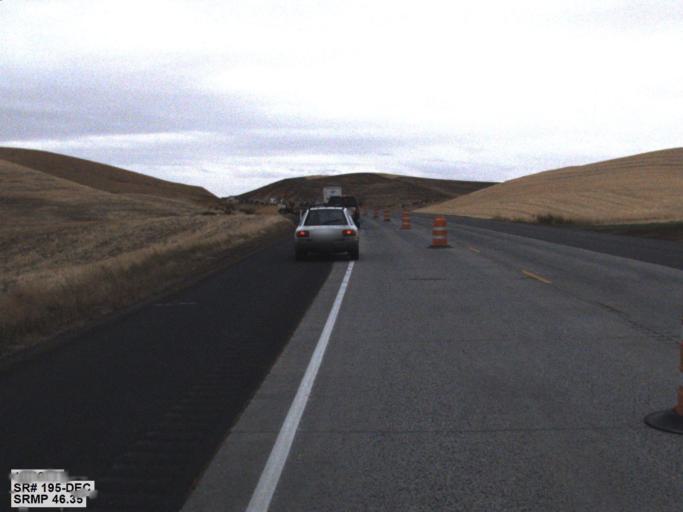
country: US
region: Washington
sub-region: Whitman County
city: Colfax
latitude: 46.9837
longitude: -117.3456
